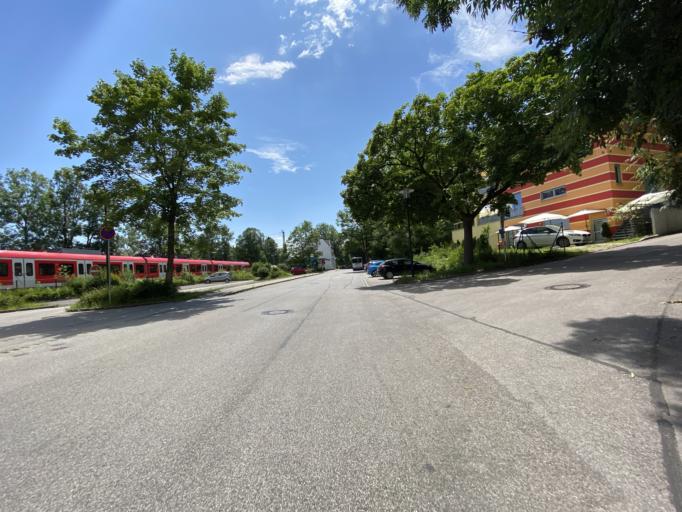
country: DE
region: Bavaria
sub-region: Upper Bavaria
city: Seefeld
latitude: 48.0416
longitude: 11.1984
